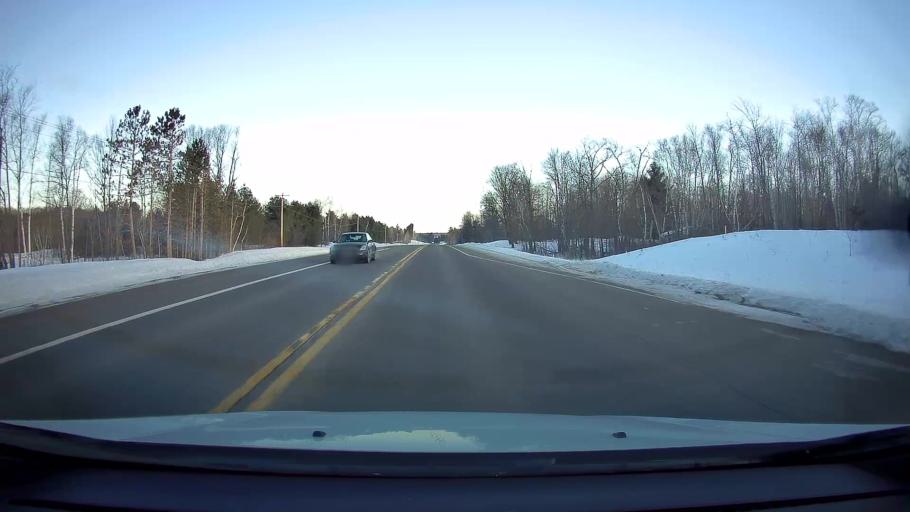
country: US
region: Wisconsin
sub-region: Barron County
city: Cumberland
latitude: 45.5891
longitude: -92.0176
